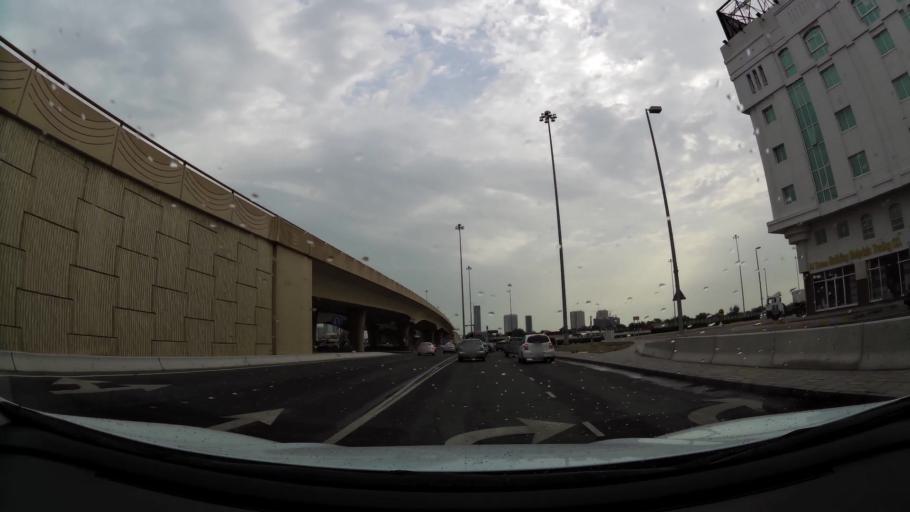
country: AE
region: Abu Dhabi
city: Abu Dhabi
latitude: 24.4797
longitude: 54.3857
